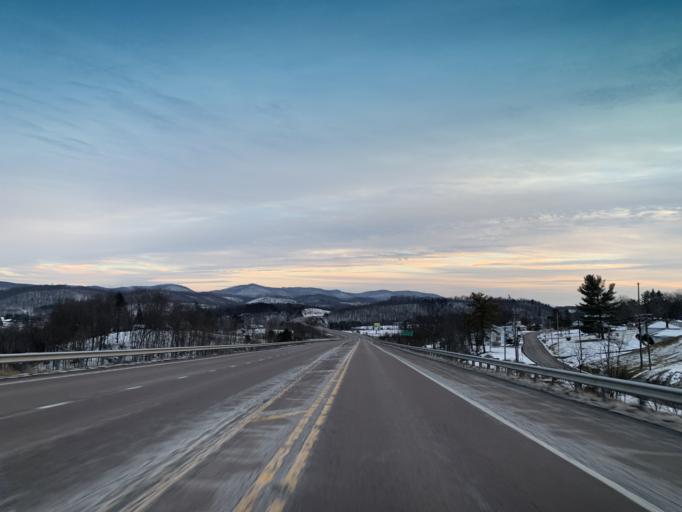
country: US
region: Maryland
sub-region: Allegany County
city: Cumberland
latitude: 39.7192
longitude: -78.7036
